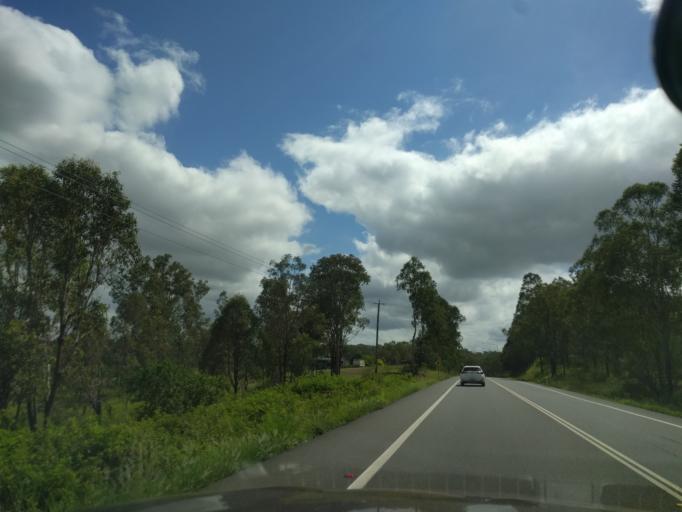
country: AU
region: Queensland
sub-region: Logan
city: Cedar Vale
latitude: -27.8868
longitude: 152.9781
